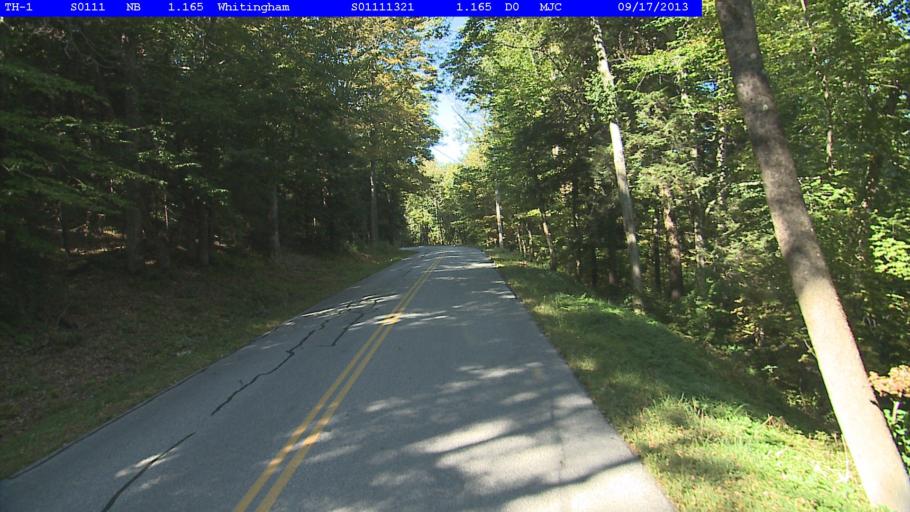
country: US
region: Massachusetts
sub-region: Franklin County
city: Charlemont
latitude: 42.7528
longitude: -72.8192
